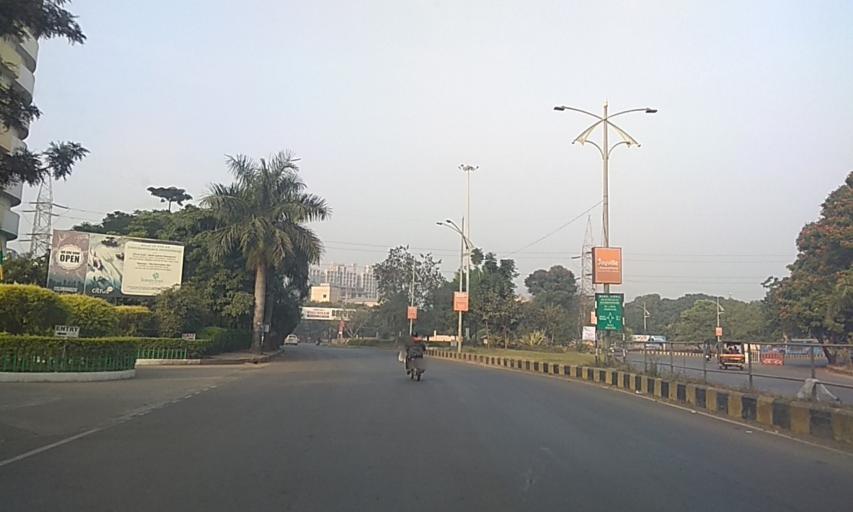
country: IN
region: Maharashtra
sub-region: Pune Division
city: Pimpri
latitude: 18.5860
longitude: 73.7347
